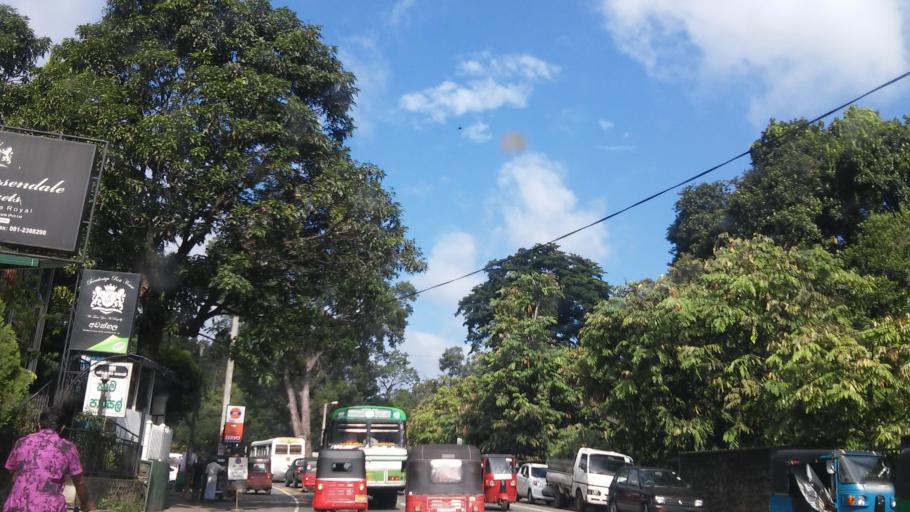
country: LK
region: Central
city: Kandy
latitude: 7.2683
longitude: 80.5977
